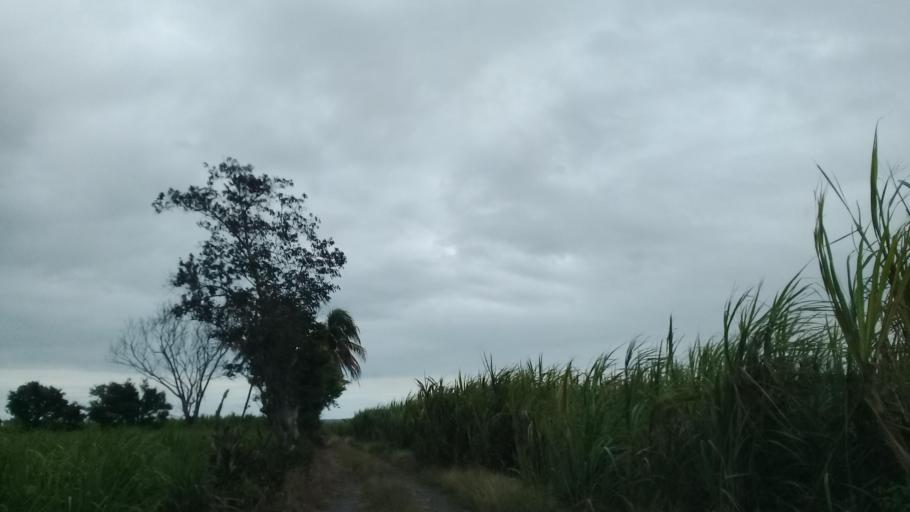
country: MX
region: Veracruz
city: Ursulo Galvan
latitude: 19.3831
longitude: -96.3591
